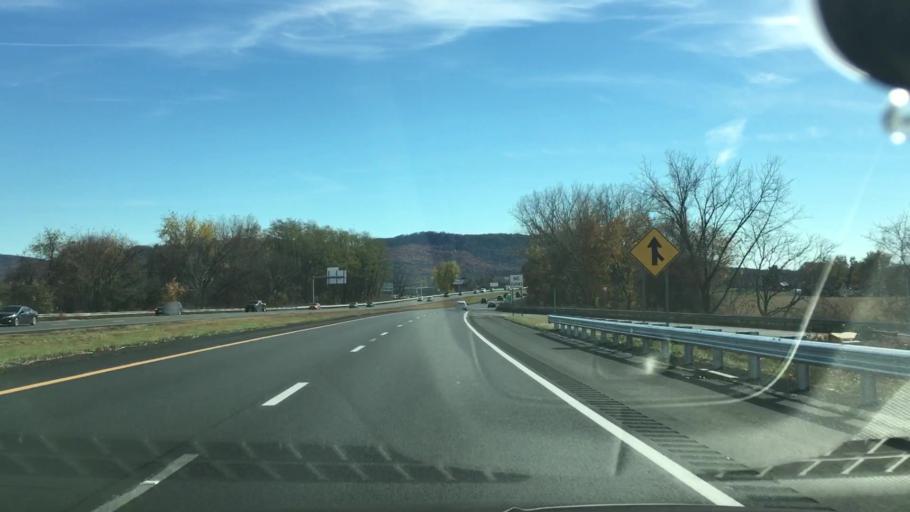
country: US
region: Massachusetts
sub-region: Hampshire County
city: Northampton
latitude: 42.3321
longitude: -72.6204
